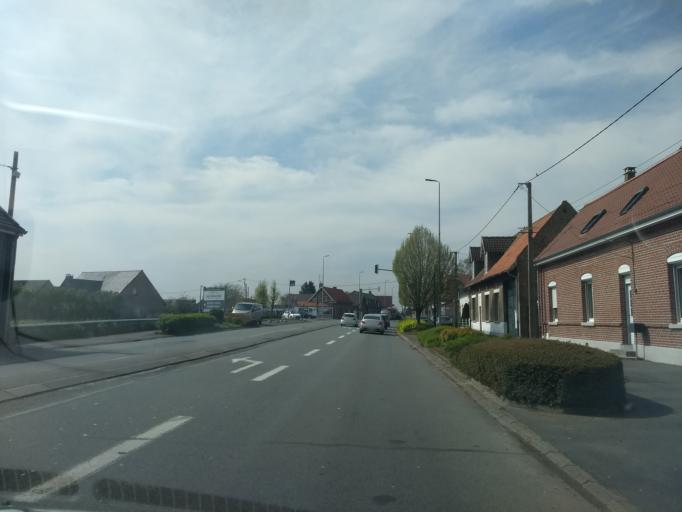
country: FR
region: Nord-Pas-de-Calais
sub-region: Departement du Pas-de-Calais
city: Biache-Saint-Vaast
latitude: 50.3344
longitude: 2.9338
